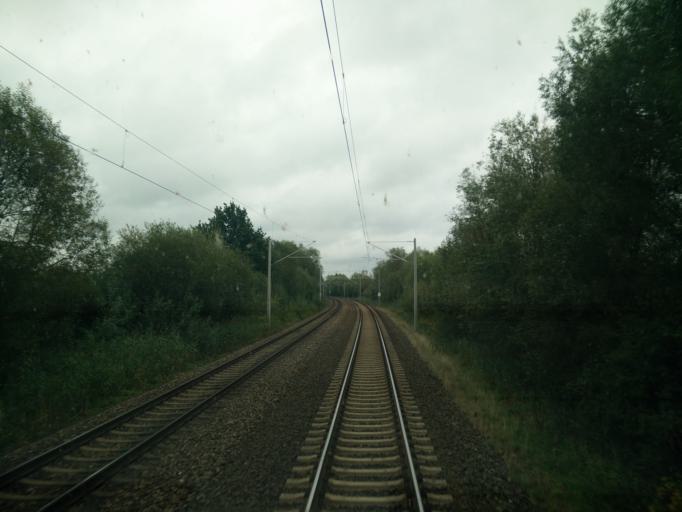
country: DE
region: Brandenburg
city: Luebben
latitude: 51.9602
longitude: 13.8246
